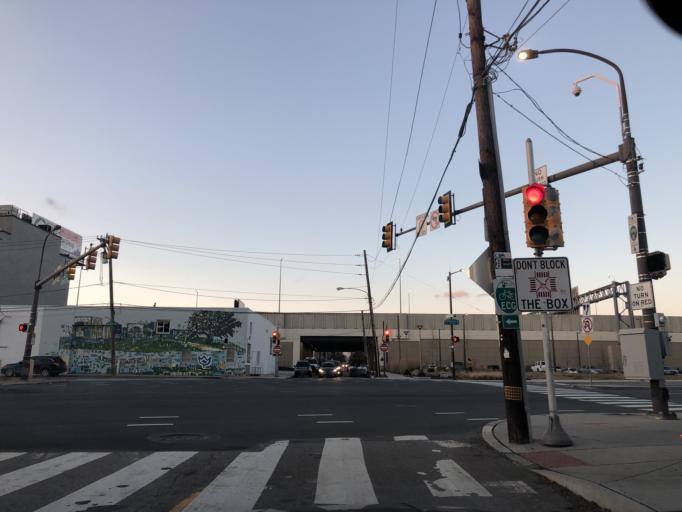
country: US
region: Pennsylvania
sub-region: Philadelphia County
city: Philadelphia
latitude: 39.9672
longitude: -75.1288
